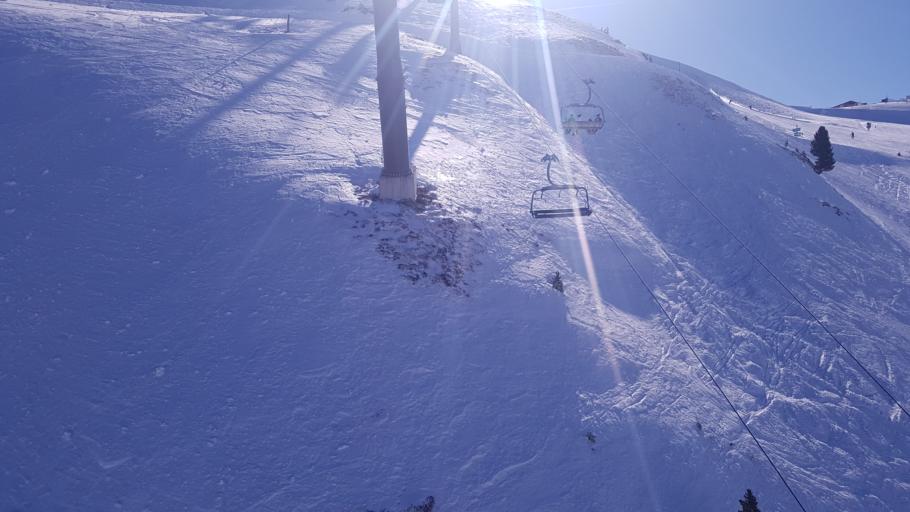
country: AT
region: Salzburg
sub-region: Politischer Bezirk Zell am See
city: Neukirchen am Grossvenediger
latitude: 47.2870
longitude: 12.2865
